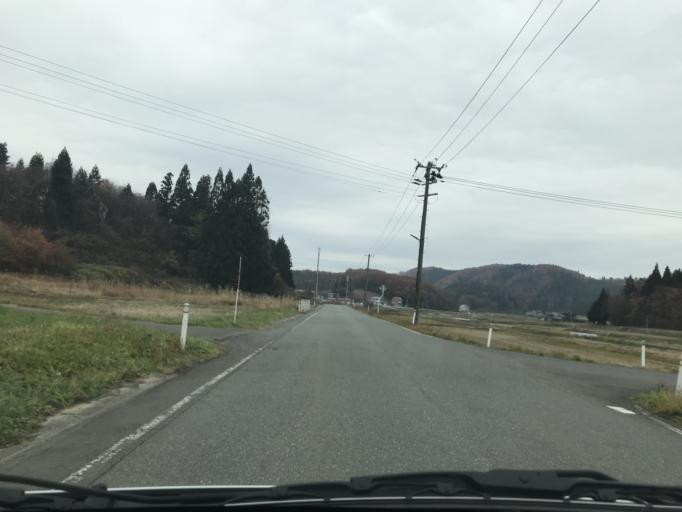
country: JP
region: Iwate
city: Kitakami
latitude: 39.2894
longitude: 141.1743
